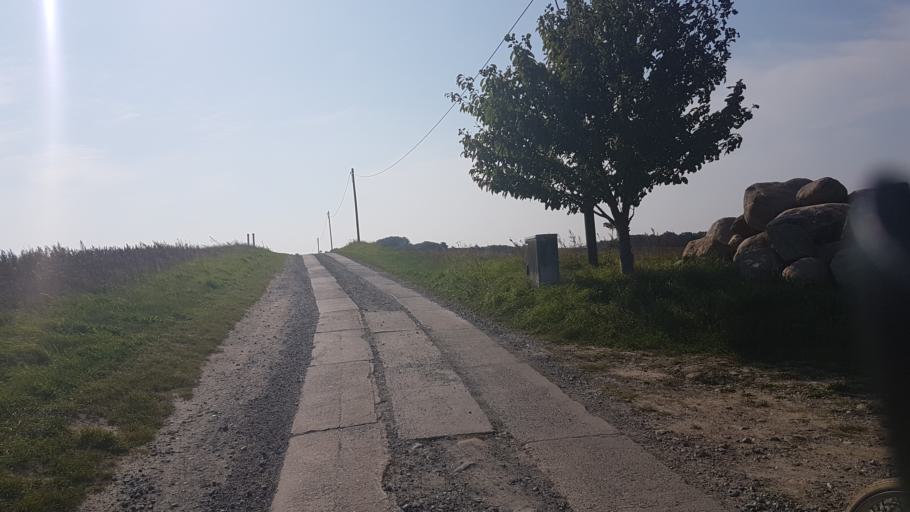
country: DE
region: Mecklenburg-Vorpommern
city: Putbus
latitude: 54.3252
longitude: 13.4559
